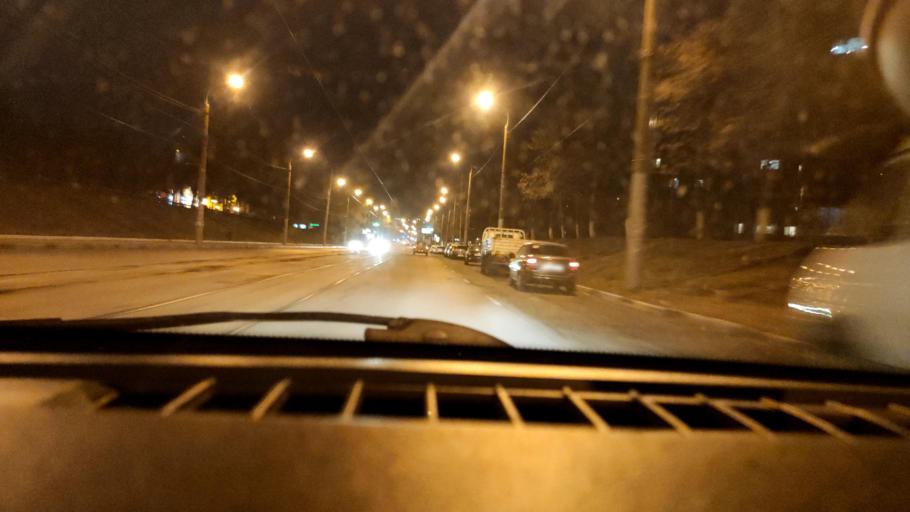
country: RU
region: Samara
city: Samara
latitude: 53.1917
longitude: 50.2029
